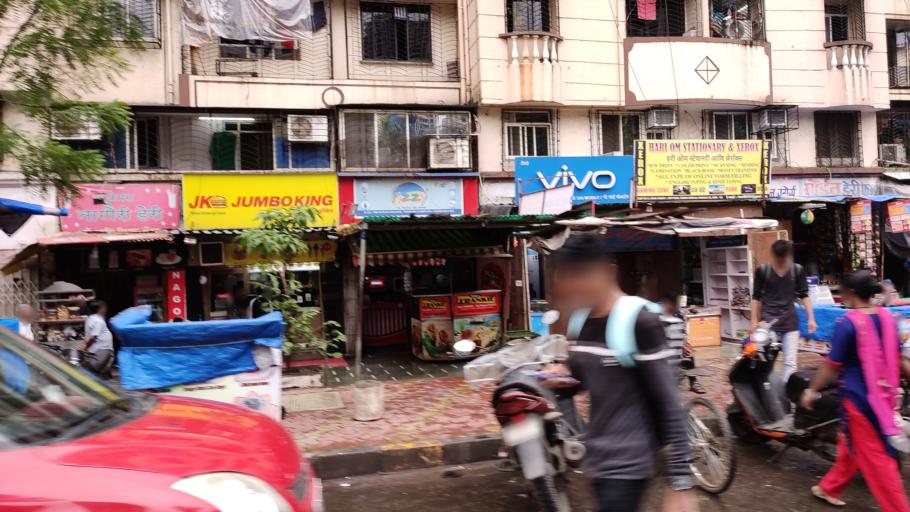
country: IN
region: Maharashtra
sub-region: Mumbai Suburban
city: Borivli
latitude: 19.2138
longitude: 72.8669
